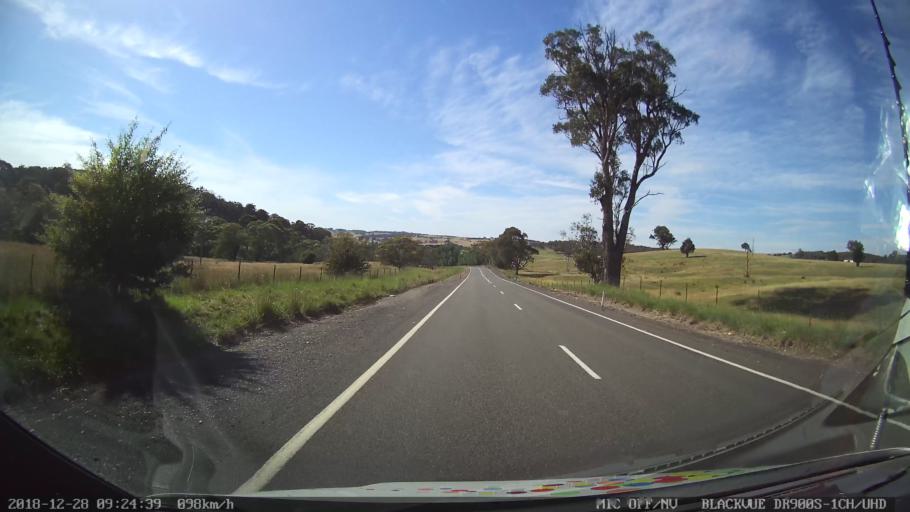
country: AU
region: New South Wales
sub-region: Upper Lachlan Shire
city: Crookwell
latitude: -34.4004
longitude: 149.3822
